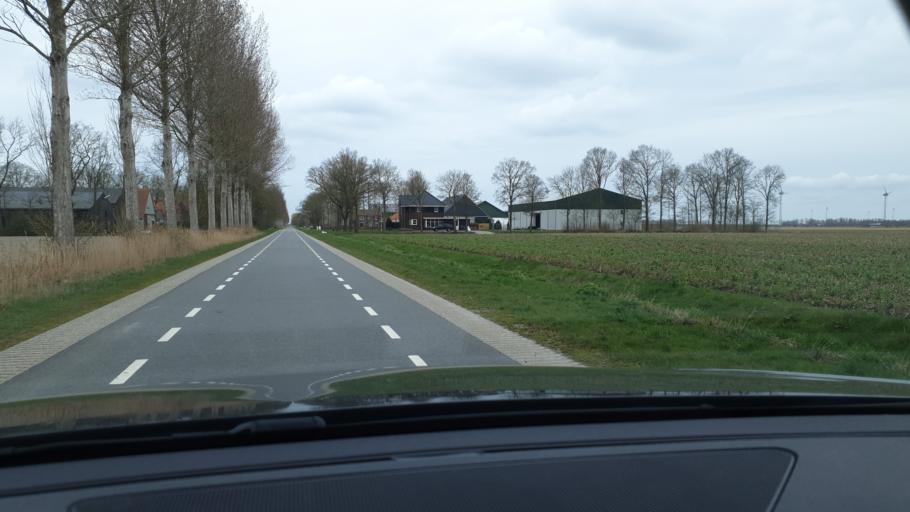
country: NL
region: Flevoland
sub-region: Gemeente Urk
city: Urk
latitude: 52.7252
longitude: 5.6349
